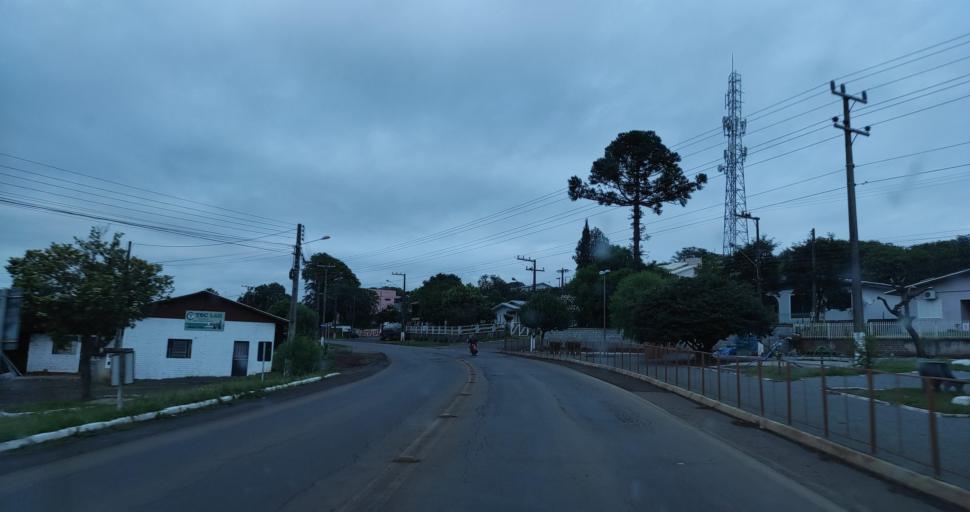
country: BR
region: Santa Catarina
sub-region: Xanxere
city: Xanxere
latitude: -26.7360
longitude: -52.3923
